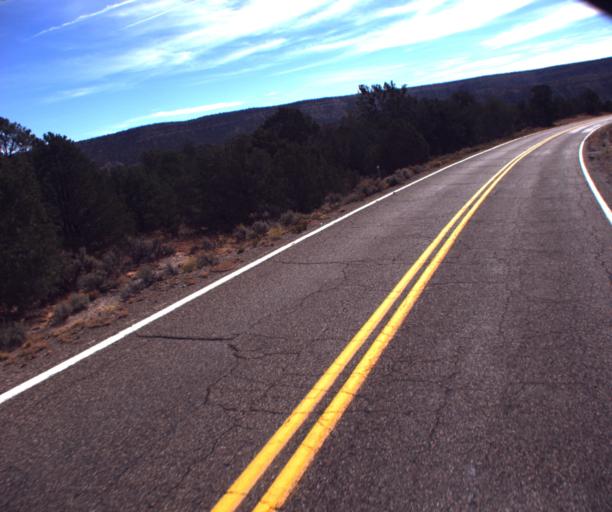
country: US
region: Arizona
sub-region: Navajo County
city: Kayenta
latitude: 36.5858
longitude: -110.4910
